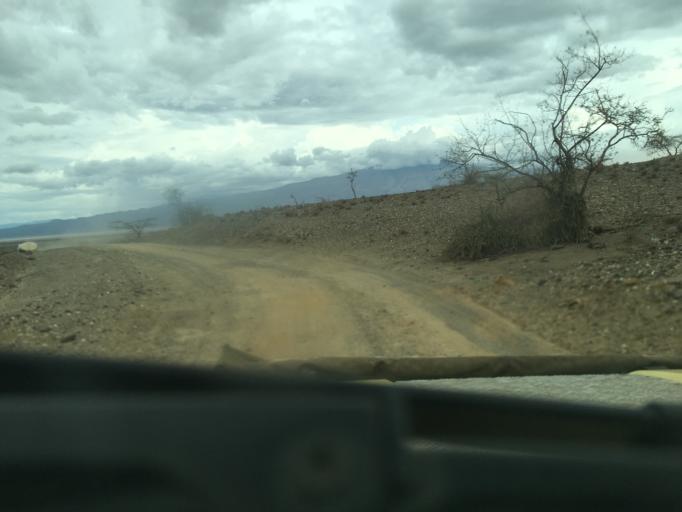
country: KE
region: Kajiado
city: Magadi
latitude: -2.5080
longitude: 35.8828
